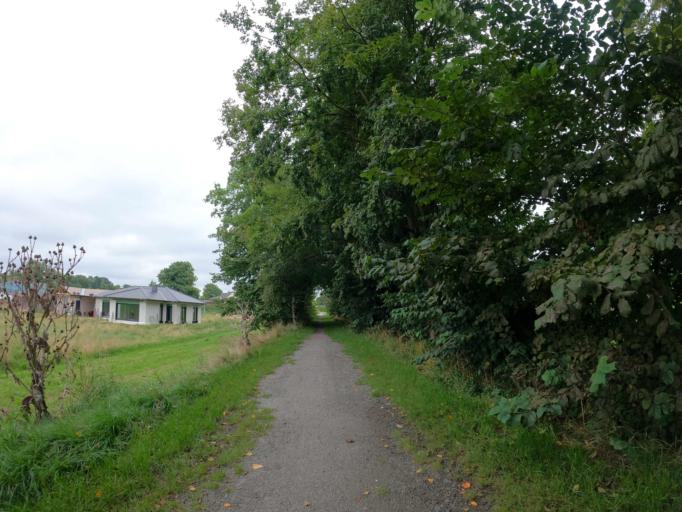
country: DE
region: Mecklenburg-Vorpommern
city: Garz
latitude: 54.3260
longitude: 13.3525
